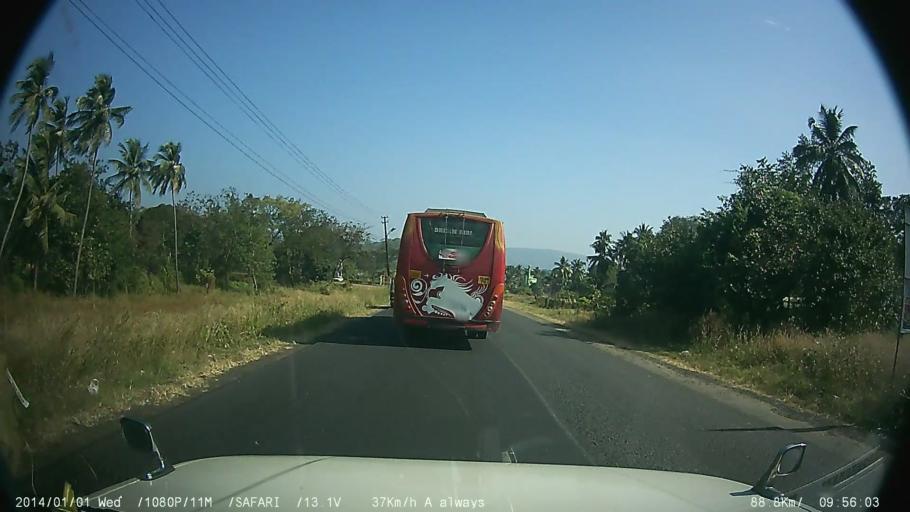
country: IN
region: Kerala
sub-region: Thrissur District
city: Trichur
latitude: 10.5421
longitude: 76.2875
